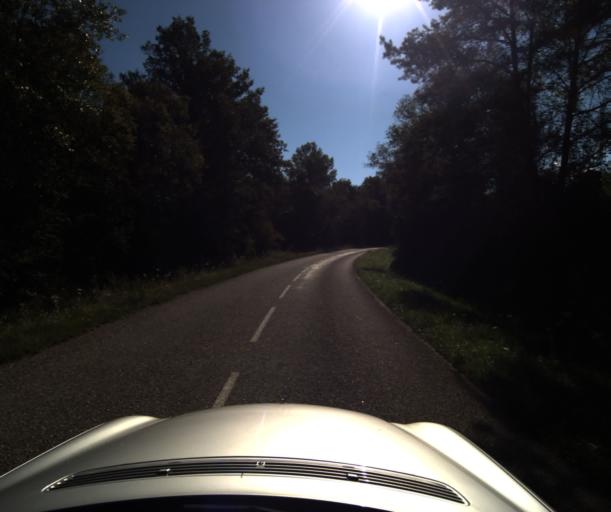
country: FR
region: Languedoc-Roussillon
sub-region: Departement de l'Aude
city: Chalabre
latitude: 42.9685
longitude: 1.9478
